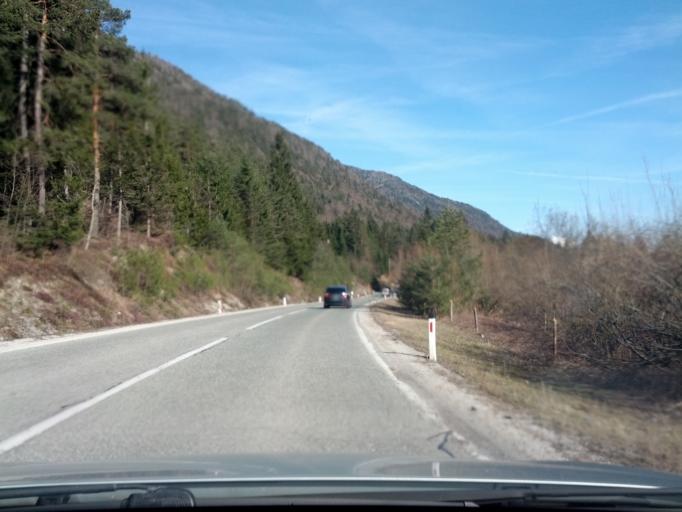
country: SI
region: Kranjska Gora
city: Mojstrana
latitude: 46.4791
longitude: 13.8811
